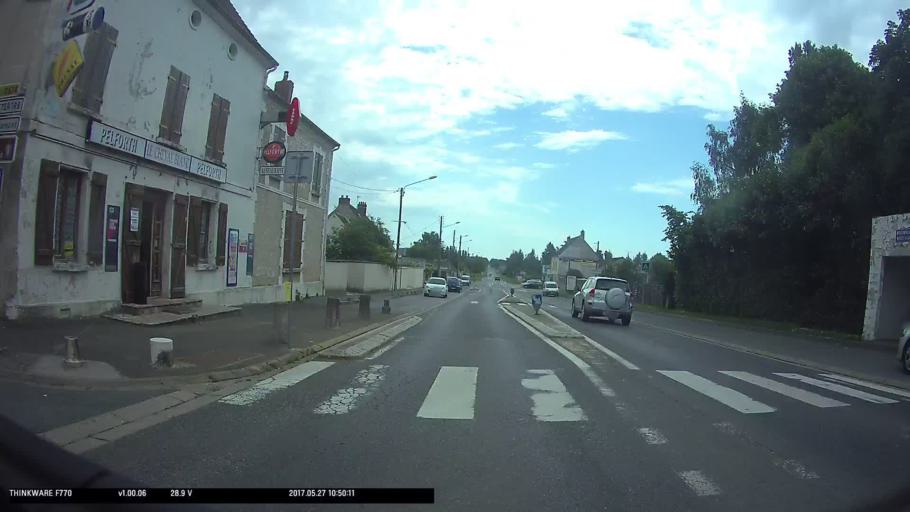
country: FR
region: Ile-de-France
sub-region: Departement du Val-d'Oise
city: Chars
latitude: 49.1778
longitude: 1.9051
